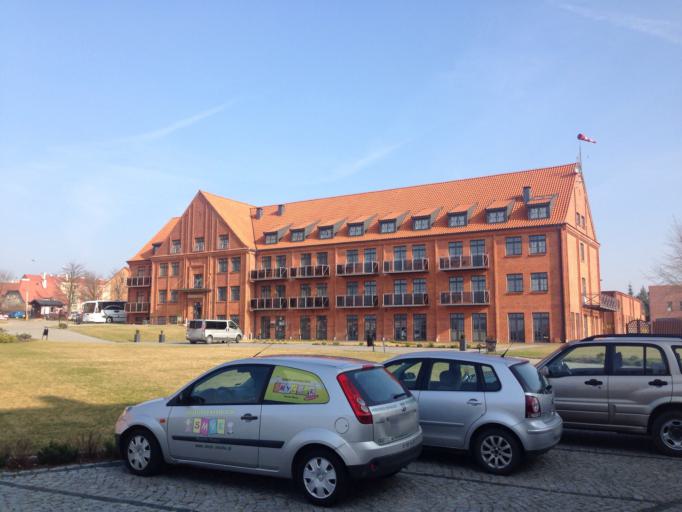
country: PL
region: Pomeranian Voivodeship
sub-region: Powiat tczewski
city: Gniew
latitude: 53.8337
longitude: 18.8292
